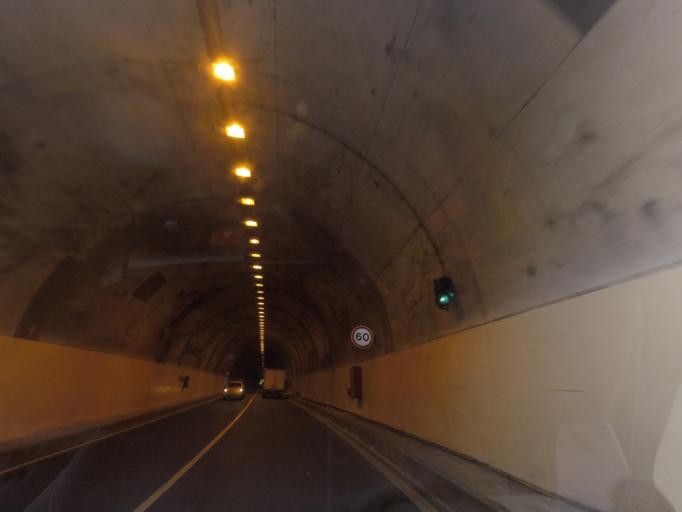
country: PT
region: Madeira
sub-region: Calheta
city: Estreito da Calheta
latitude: 32.7318
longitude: -17.1801
